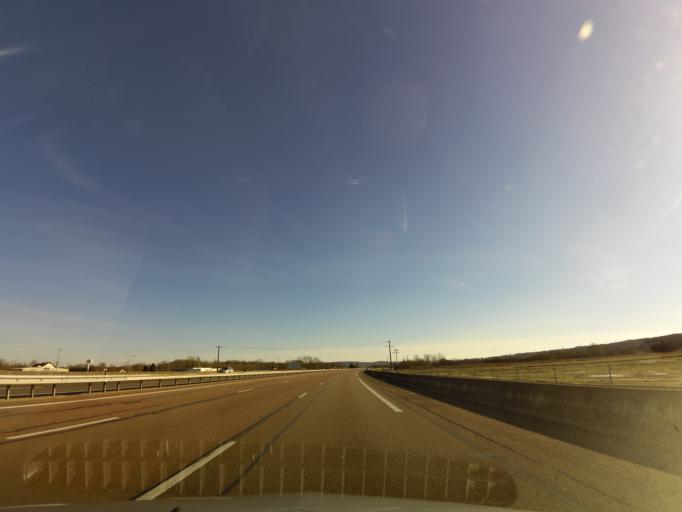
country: FR
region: Bourgogne
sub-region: Departement de l'Yonne
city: Appoigny
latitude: 47.8623
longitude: 3.5318
